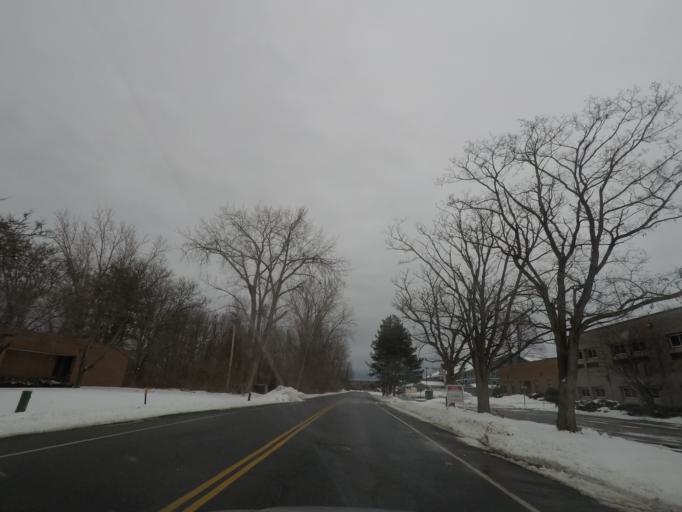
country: US
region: New York
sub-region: Albany County
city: Roessleville
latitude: 42.7156
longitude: -73.8035
